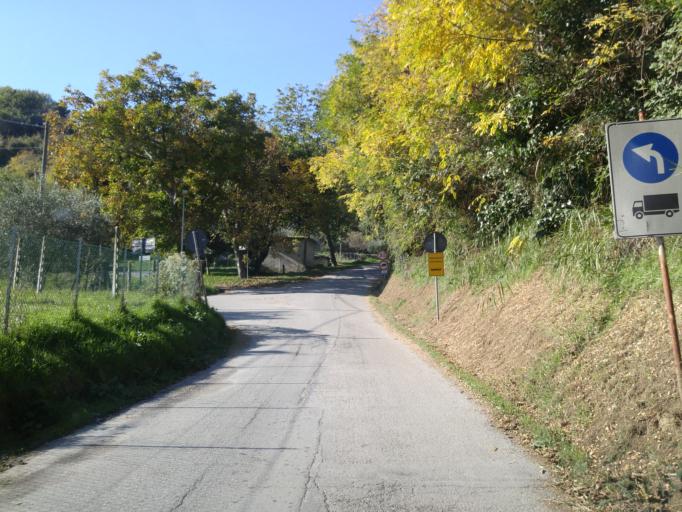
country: IT
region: The Marches
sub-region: Provincia di Pesaro e Urbino
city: Tavernelle
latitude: 43.7337
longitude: 12.8837
